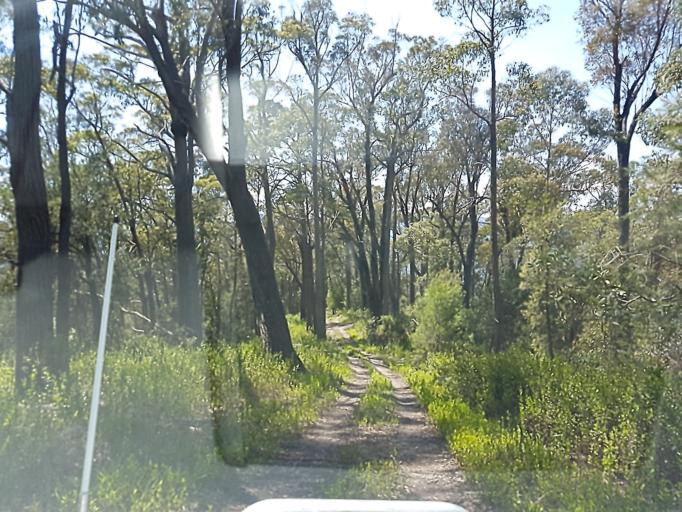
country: AU
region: Victoria
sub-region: East Gippsland
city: Lakes Entrance
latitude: -37.3112
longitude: 148.3512
